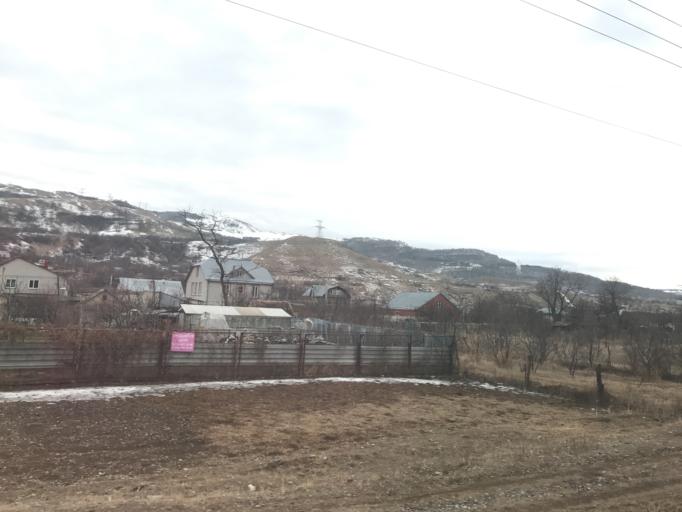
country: RU
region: Stavropol'skiy
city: Kislovodsk
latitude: 43.9538
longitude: 42.7561
